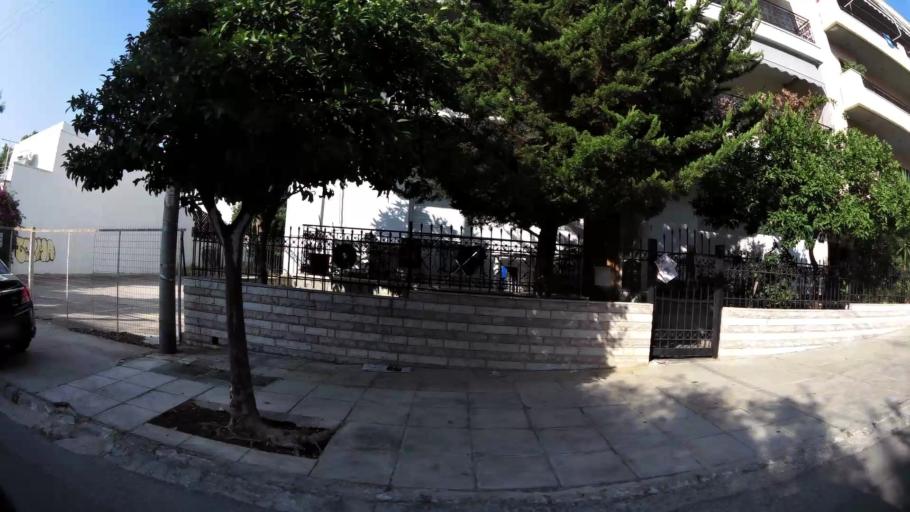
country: GR
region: Attica
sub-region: Nomarchia Athinas
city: Argyroupoli
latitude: 37.9100
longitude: 23.7518
